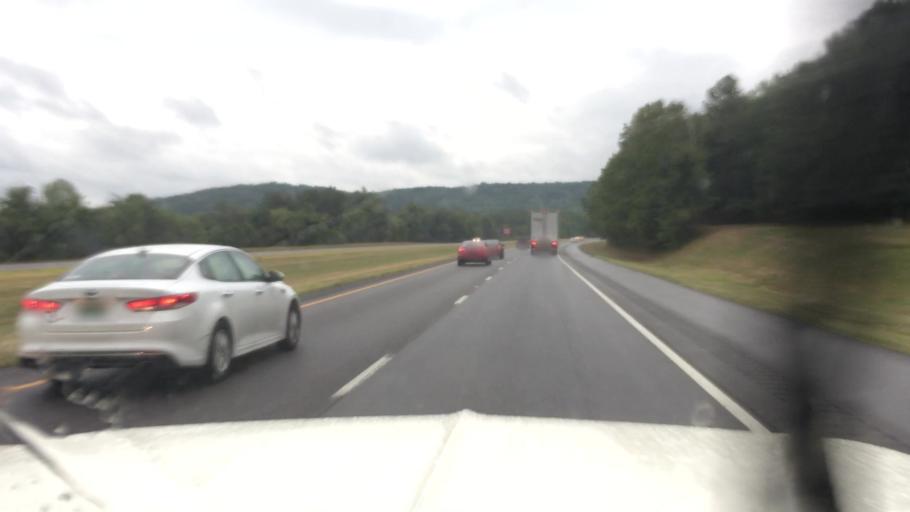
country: US
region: Alabama
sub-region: Morgan County
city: Falkville
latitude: 34.3463
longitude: -86.8924
